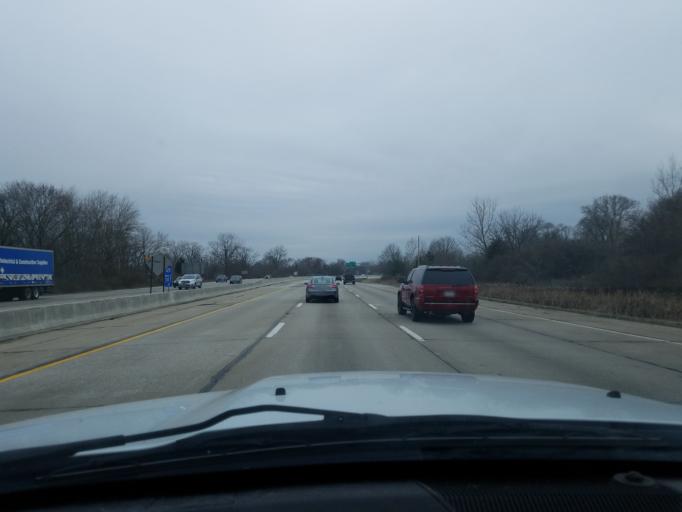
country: US
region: Indiana
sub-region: Marion County
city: Beech Grove
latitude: 39.7180
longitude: -86.1269
